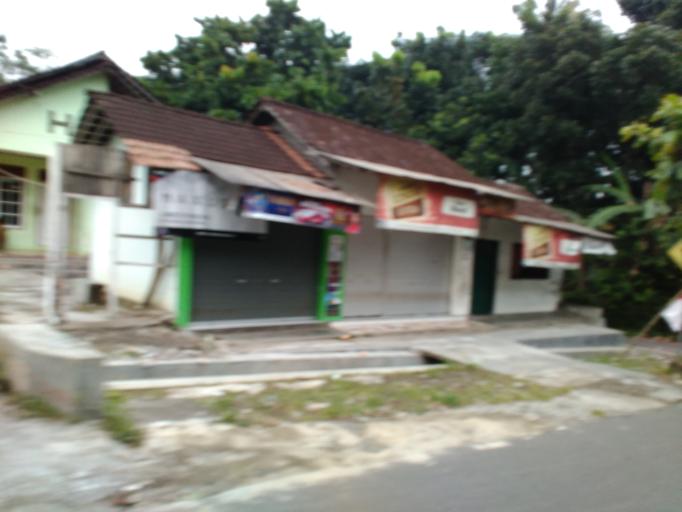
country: ID
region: Central Java
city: Boyolali
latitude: -7.5241
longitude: 110.5972
